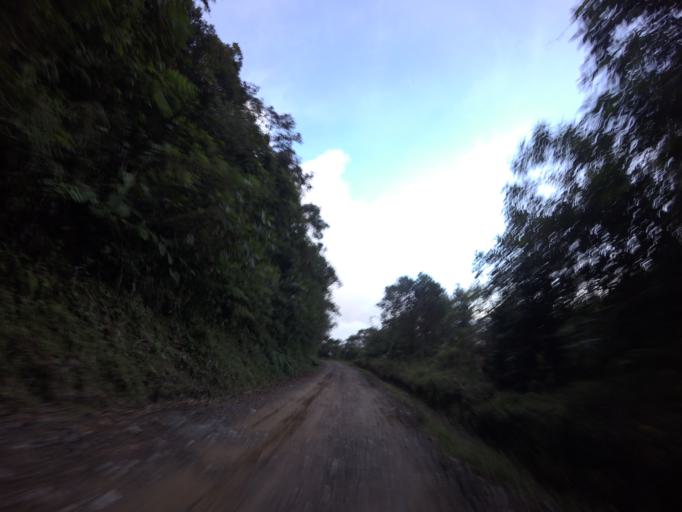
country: CO
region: Caldas
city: Pensilvania
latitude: 5.4623
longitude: -75.1192
